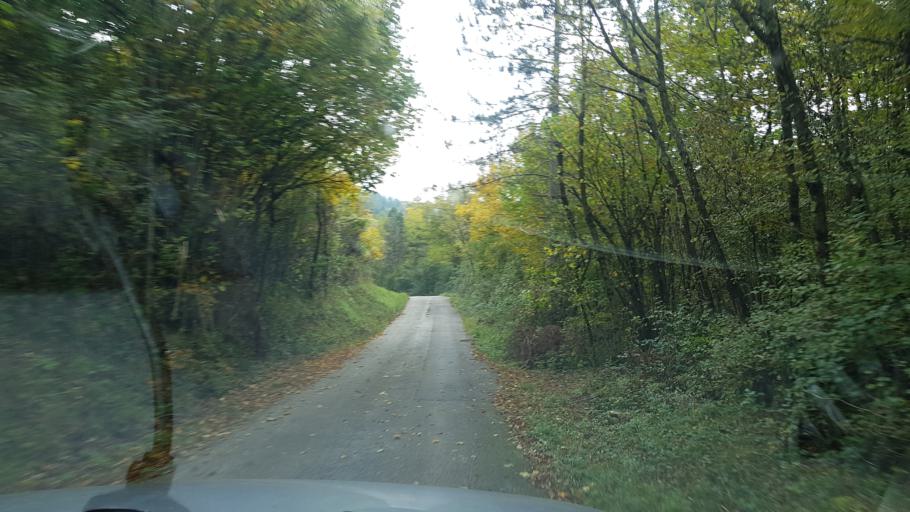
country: HR
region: Istarska
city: Buzet
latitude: 45.4343
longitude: 14.0595
